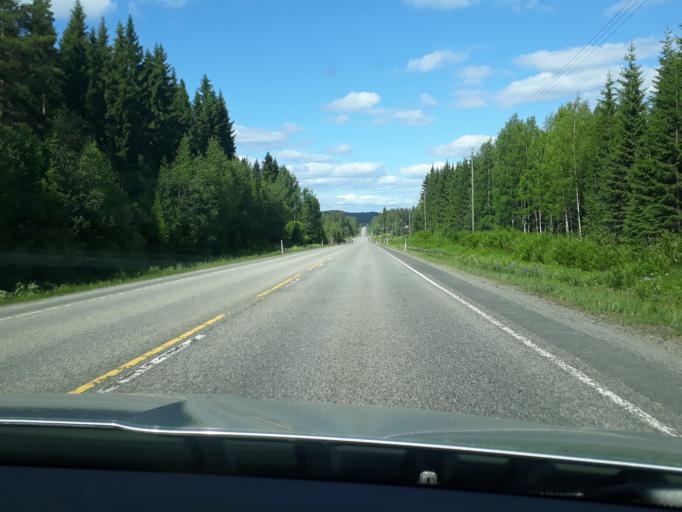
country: FI
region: Central Finland
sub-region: AEaenekoski
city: AEaenekoski
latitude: 62.6513
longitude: 25.7179
